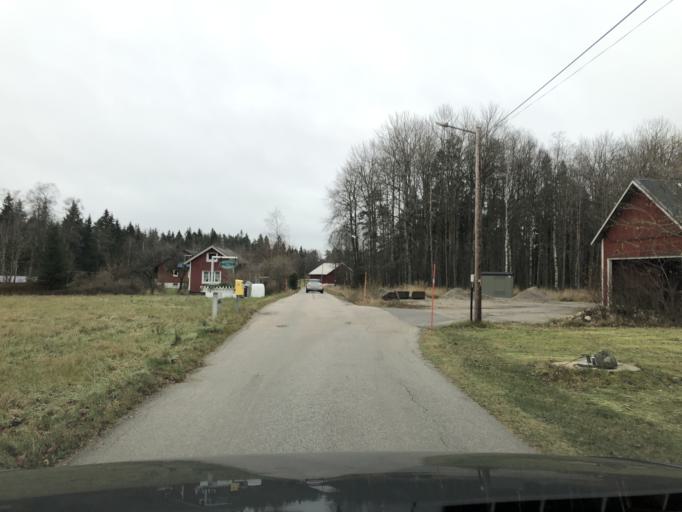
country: SE
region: Vaestra Goetaland
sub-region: Boras Kommun
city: Sjomarken
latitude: 57.7678
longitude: 12.8526
